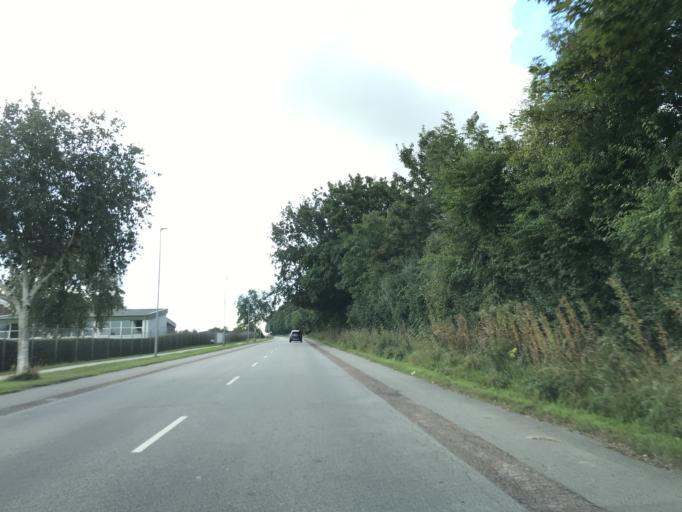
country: DK
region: South Denmark
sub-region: Haderslev Kommune
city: Haderslev
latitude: 55.2303
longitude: 9.4943
